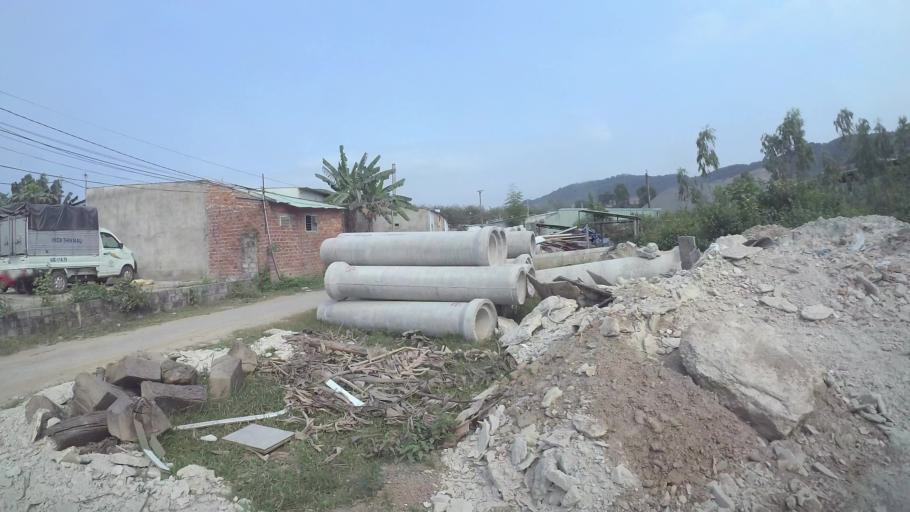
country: VN
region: Da Nang
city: Lien Chieu
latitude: 16.0457
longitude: 108.1463
